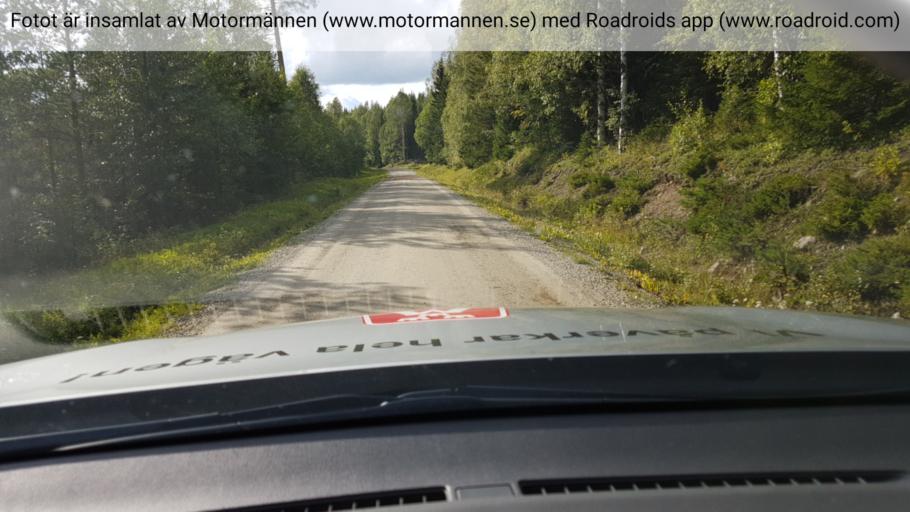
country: SE
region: Jaemtland
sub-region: Ragunda Kommun
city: Hammarstrand
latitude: 63.2836
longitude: 15.9863
